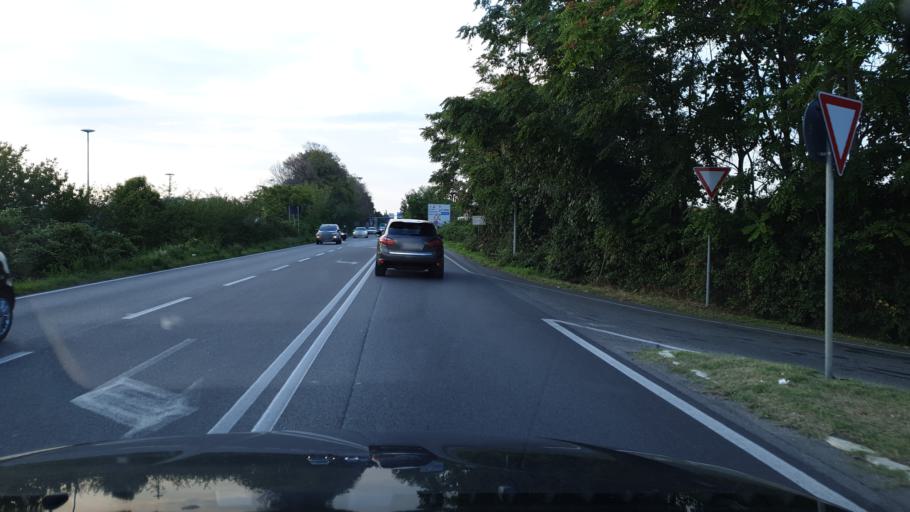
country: IT
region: Emilia-Romagna
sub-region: Provincia di Rimini
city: Rivazzurra
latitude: 44.0214
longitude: 12.6231
